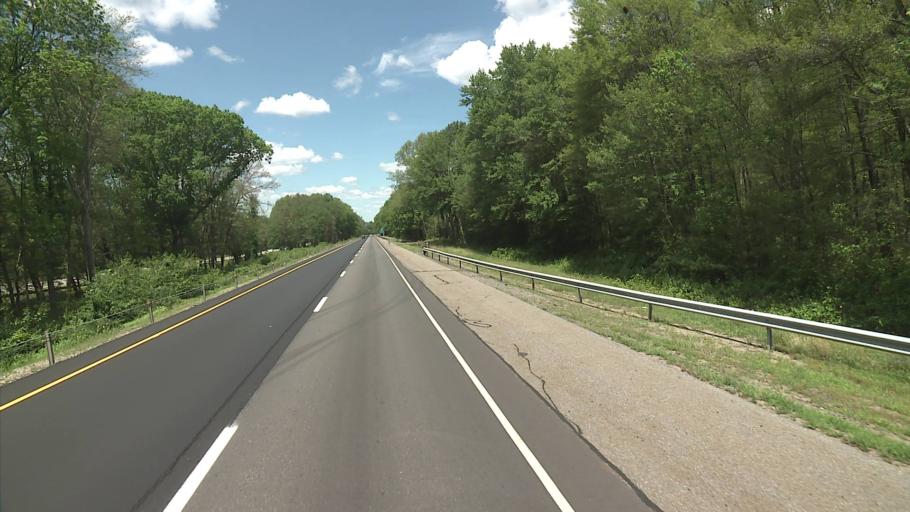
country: US
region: Connecticut
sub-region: Windham County
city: Killingly Center
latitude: 41.8223
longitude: -71.8709
